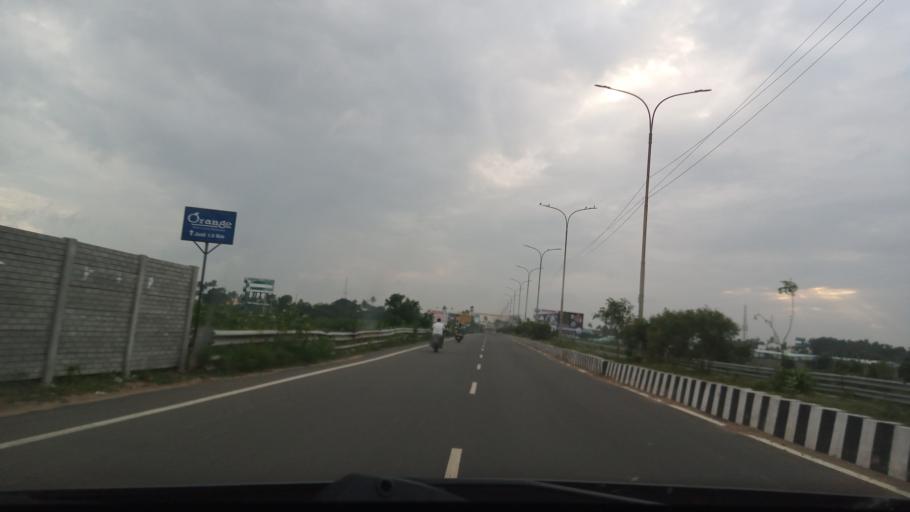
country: IN
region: Pondicherry
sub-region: Puducherry
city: Puducherry
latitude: 11.9633
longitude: 79.8333
